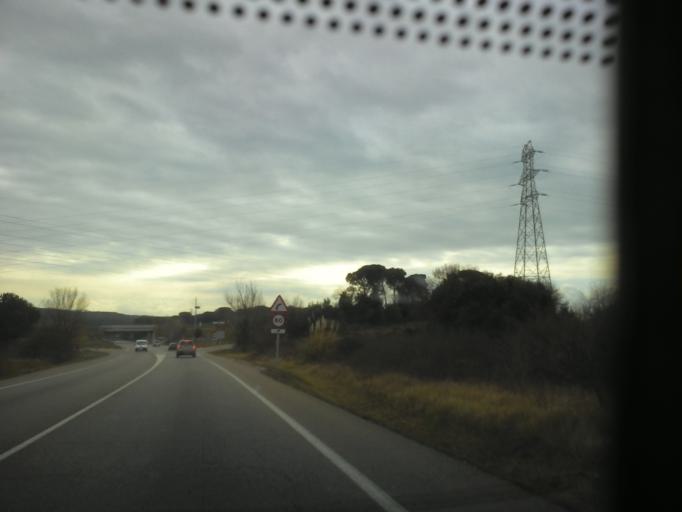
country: ES
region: Catalonia
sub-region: Provincia de Girona
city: Fornells de la Selva
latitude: 41.9432
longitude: 2.8160
